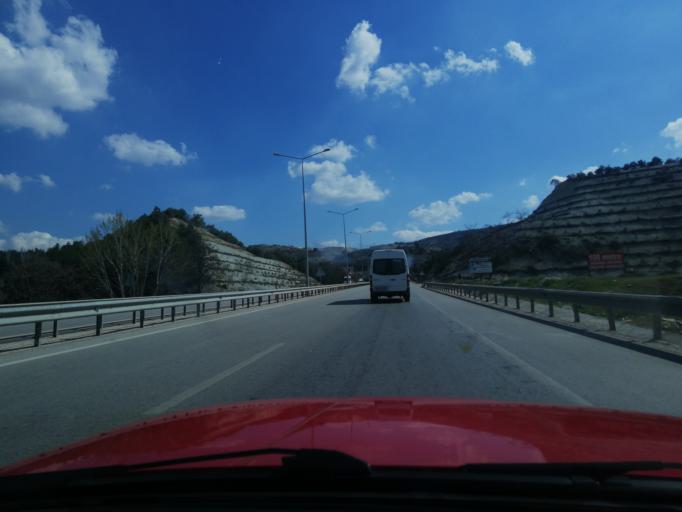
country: TR
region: Burdur
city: Burdur
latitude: 37.7056
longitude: 30.3061
